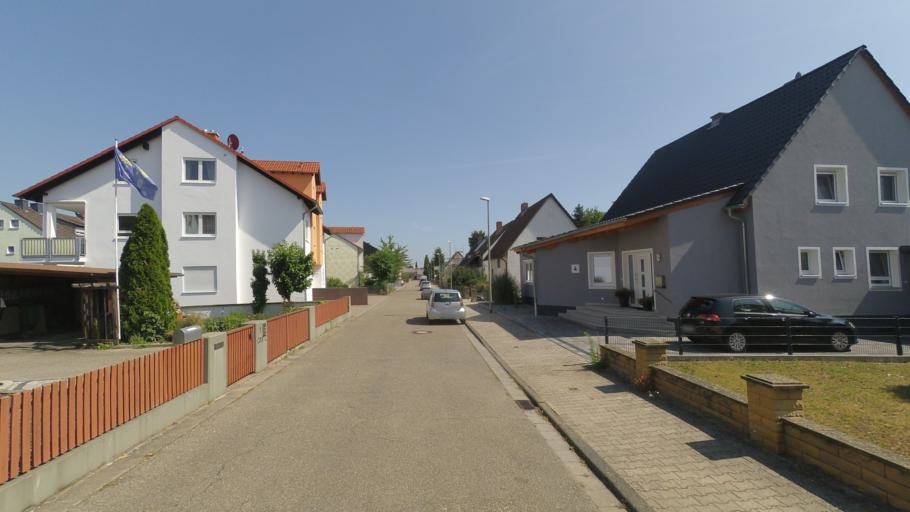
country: DE
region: Rheinland-Pfalz
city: Mutterstadt
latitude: 49.4442
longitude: 8.3617
